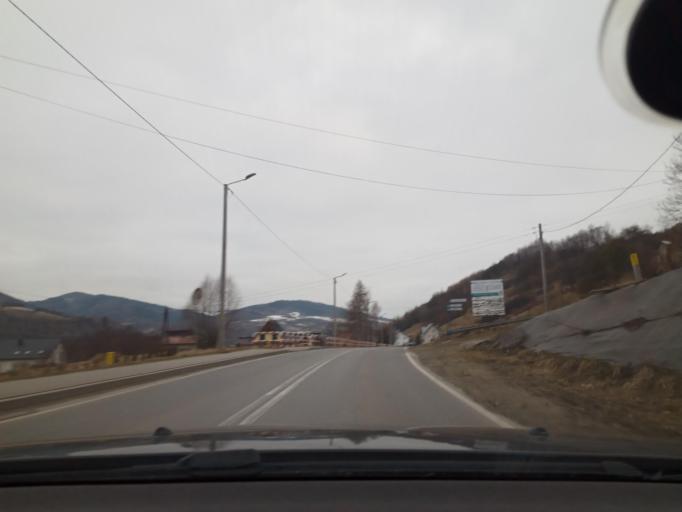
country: PL
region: Lesser Poland Voivodeship
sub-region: Powiat nowotarski
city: Ochotnica Dolna
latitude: 49.5457
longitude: 20.3858
